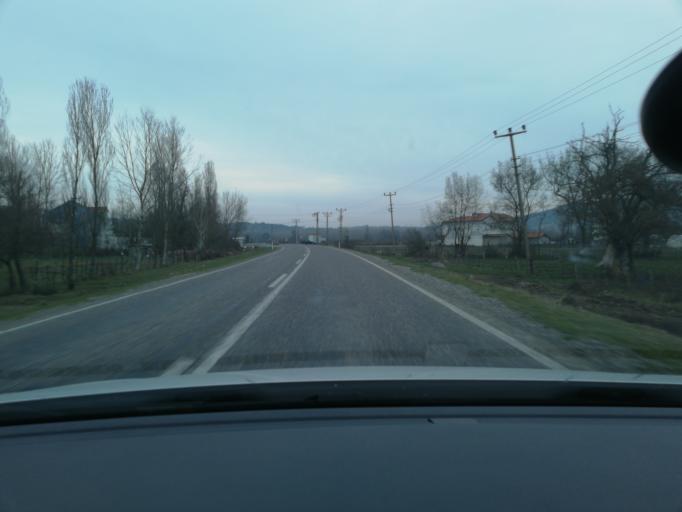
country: TR
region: Zonguldak
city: Saltukova
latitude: 41.5114
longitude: 32.1026
